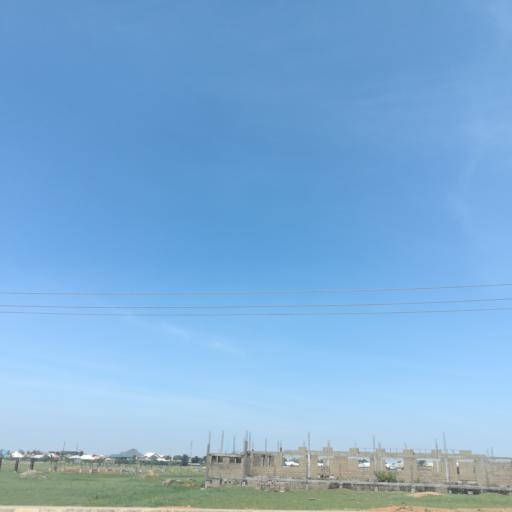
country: NG
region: Plateau
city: Bukuru
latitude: 9.7885
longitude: 8.8731
